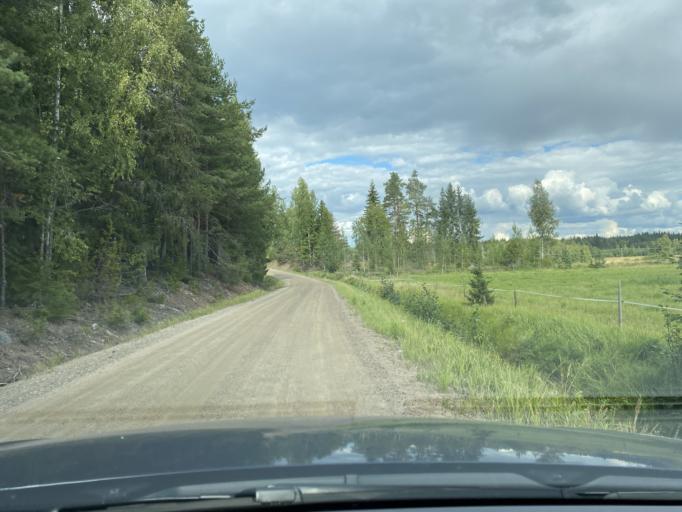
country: FI
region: Haeme
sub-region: Forssa
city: Humppila
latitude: 61.0684
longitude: 23.2700
